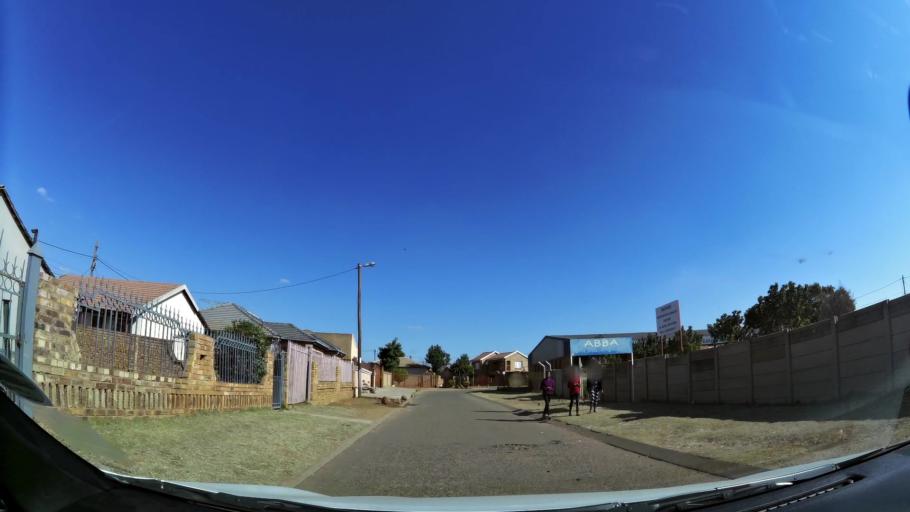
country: ZA
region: Gauteng
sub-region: City of Tshwane Metropolitan Municipality
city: Cullinan
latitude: -25.7103
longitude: 28.3959
